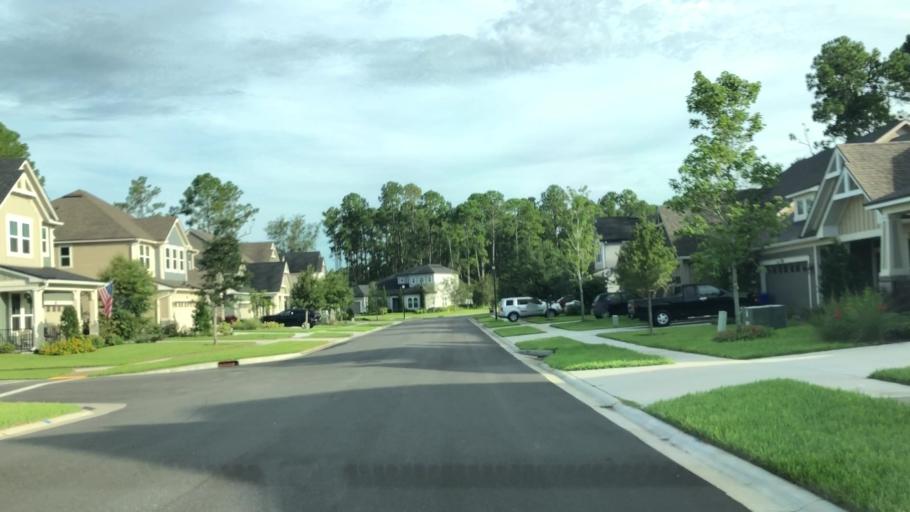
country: US
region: Florida
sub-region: Saint Johns County
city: Palm Valley
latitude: 30.1312
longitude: -81.4244
